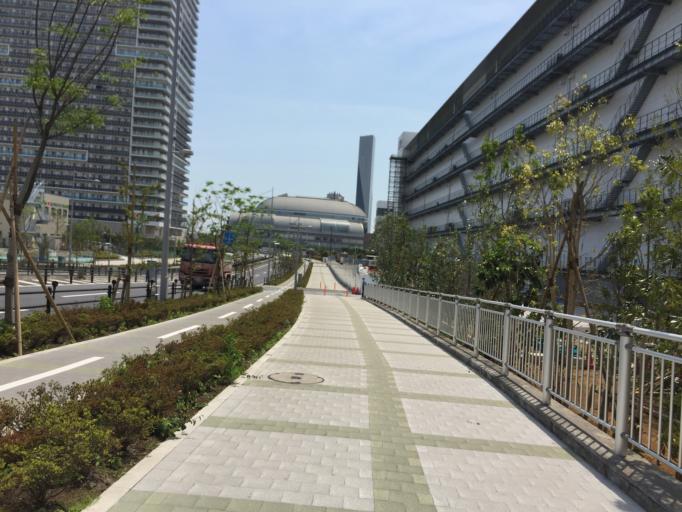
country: JP
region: Tokyo
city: Tokyo
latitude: 35.6374
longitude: 139.7803
